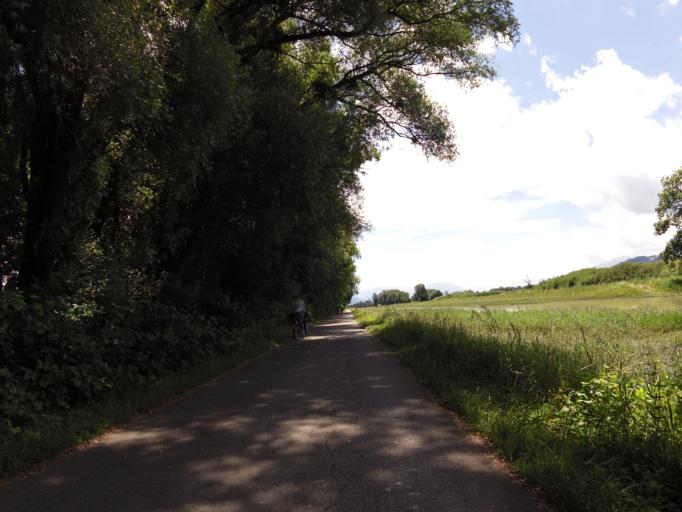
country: AT
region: Vorarlberg
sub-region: Politischer Bezirk Bregenz
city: Hard
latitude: 47.4869
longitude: 9.6754
